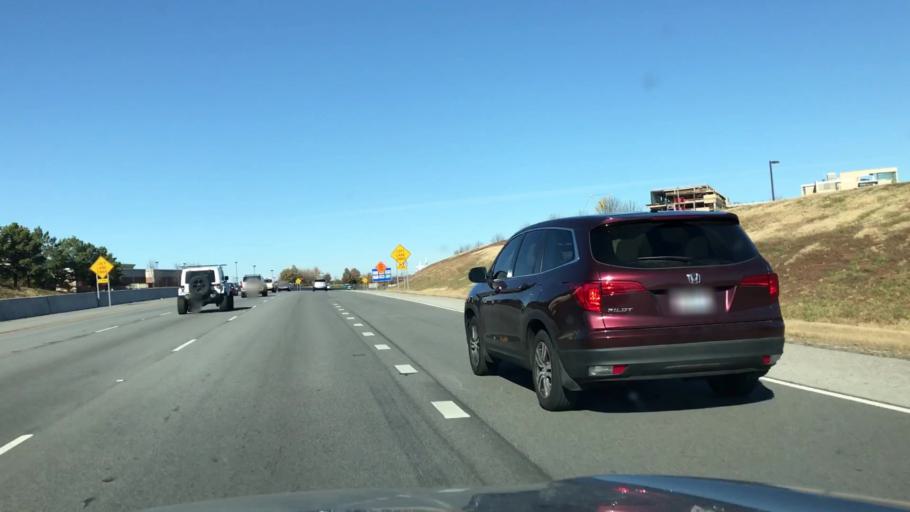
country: US
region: Arkansas
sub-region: Benton County
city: Cave Springs
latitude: 36.3050
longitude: -94.1832
